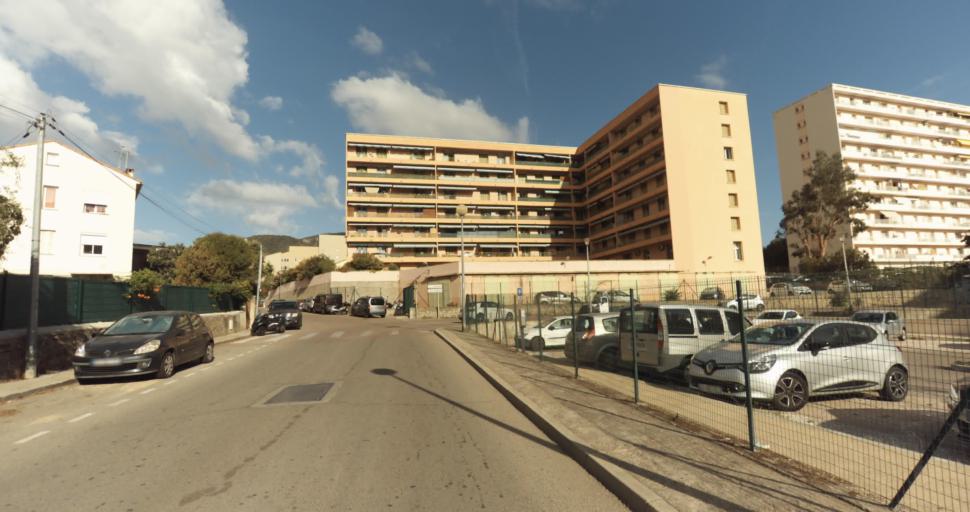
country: FR
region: Corsica
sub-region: Departement de la Corse-du-Sud
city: Ajaccio
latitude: 41.9304
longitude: 8.7323
